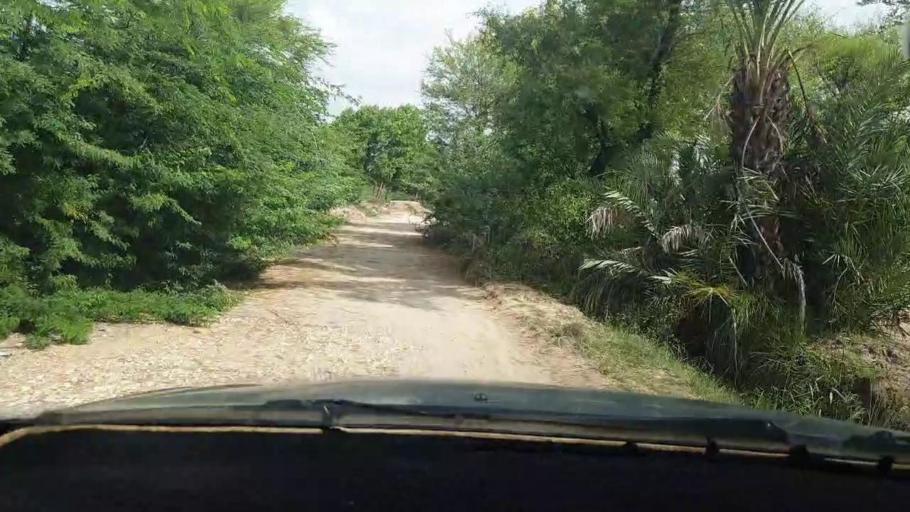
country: PK
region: Sindh
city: Tando Bago
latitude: 24.7740
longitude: 69.0248
